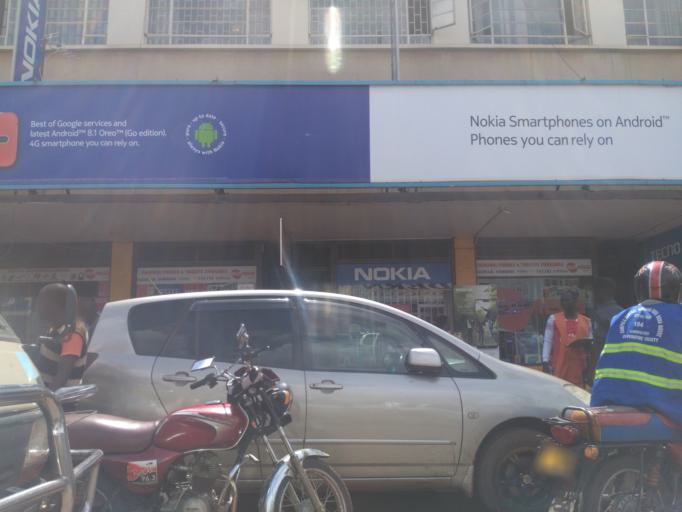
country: UG
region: Central Region
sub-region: Kampala District
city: Kampala
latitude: 0.3159
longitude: 32.5768
